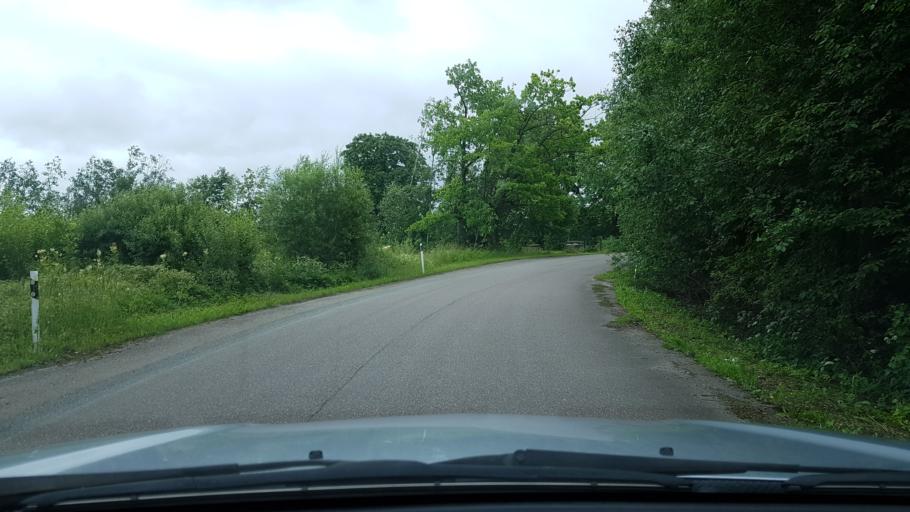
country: EE
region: Ida-Virumaa
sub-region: Narva-Joesuu linn
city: Narva-Joesuu
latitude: 59.3439
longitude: 27.9340
